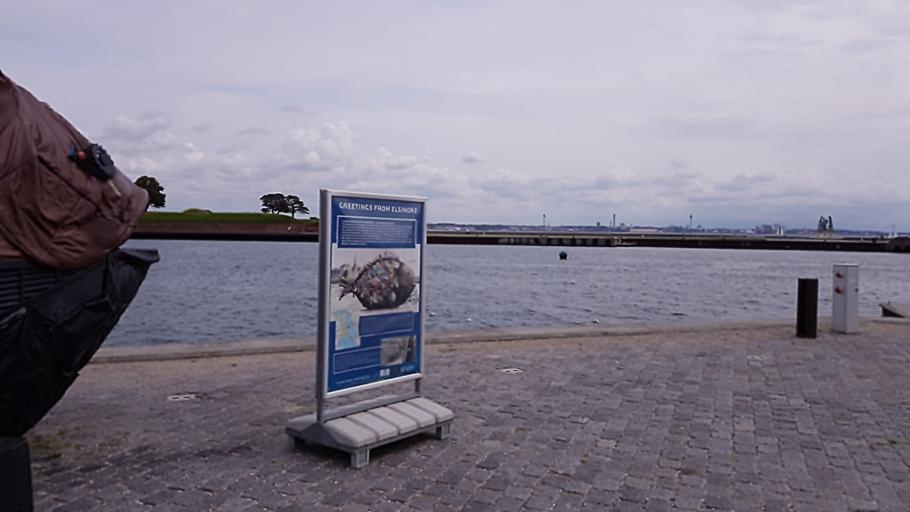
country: DK
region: Capital Region
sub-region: Helsingor Kommune
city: Helsingor
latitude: 56.0359
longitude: 12.6165
